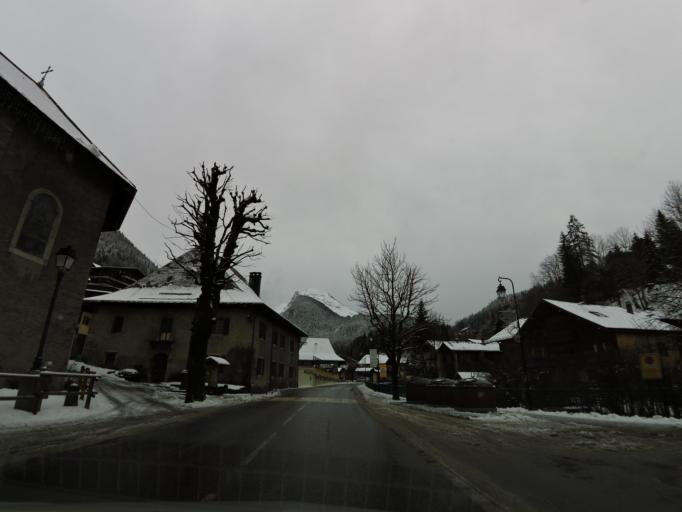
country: FR
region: Rhone-Alpes
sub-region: Departement de la Haute-Savoie
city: Morzine
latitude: 46.1786
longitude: 6.7090
